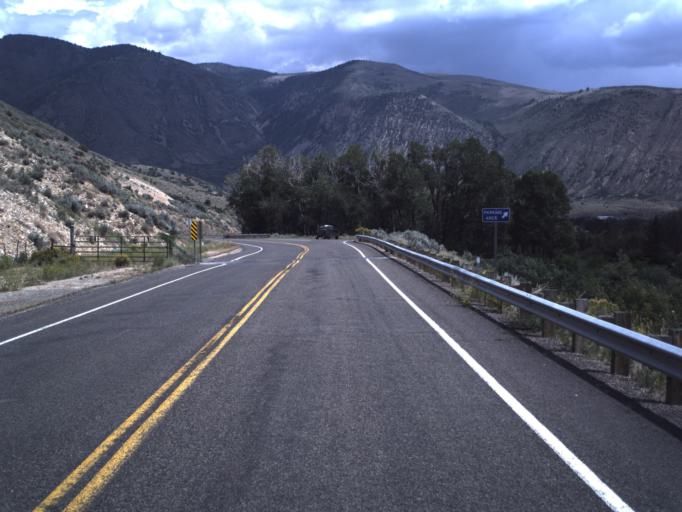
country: US
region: Utah
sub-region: Summit County
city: Francis
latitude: 40.4596
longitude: -110.8467
